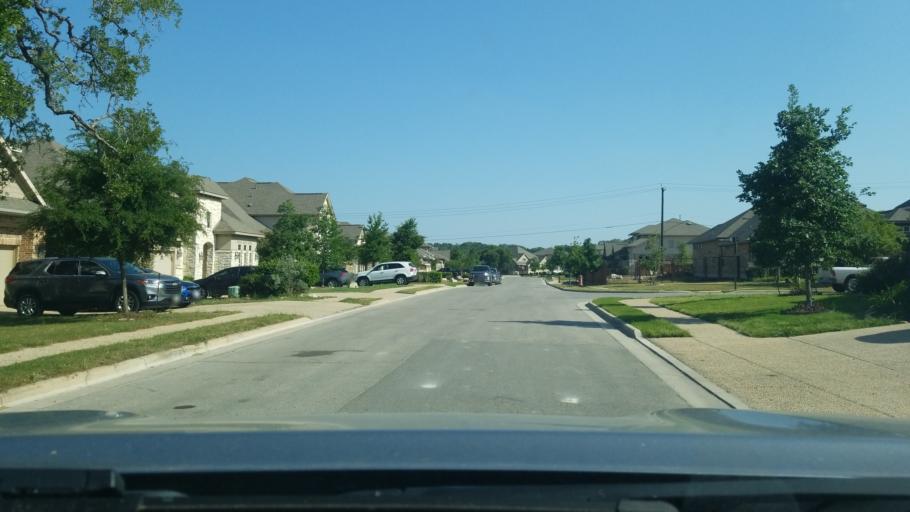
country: US
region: Texas
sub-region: Comal County
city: Bulverde
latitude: 29.7735
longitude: -98.4201
